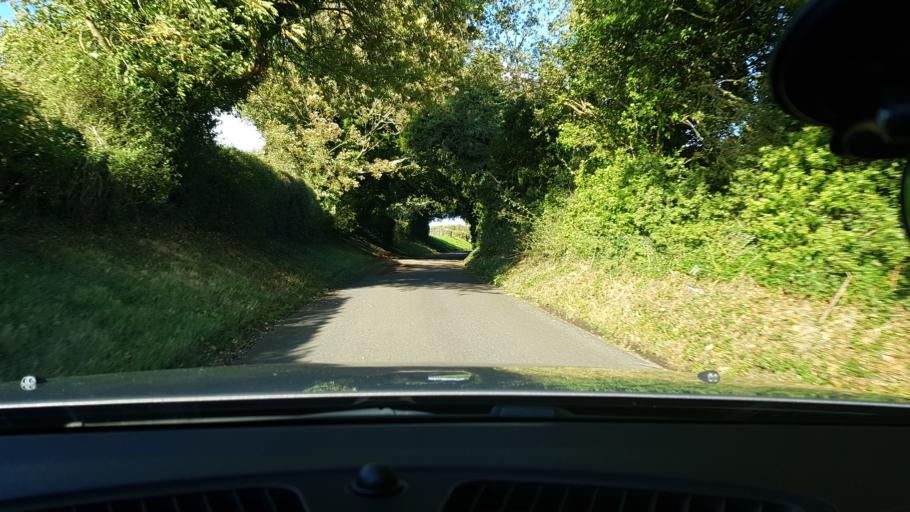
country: GB
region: England
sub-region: Wiltshire
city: Chilton Foliat
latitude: 51.4639
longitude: -1.5659
